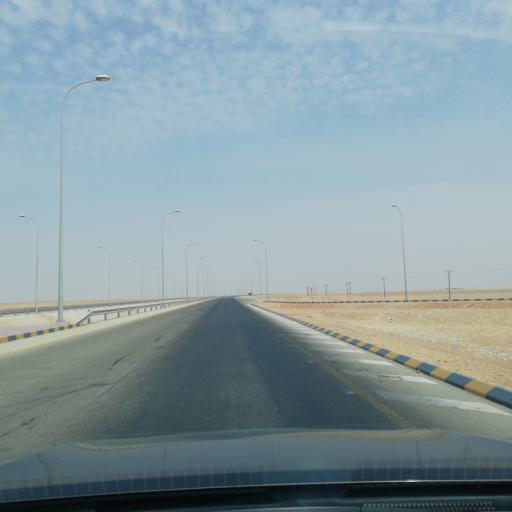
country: OM
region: Zufar
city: Salalah
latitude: 17.7067
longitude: 54.0337
